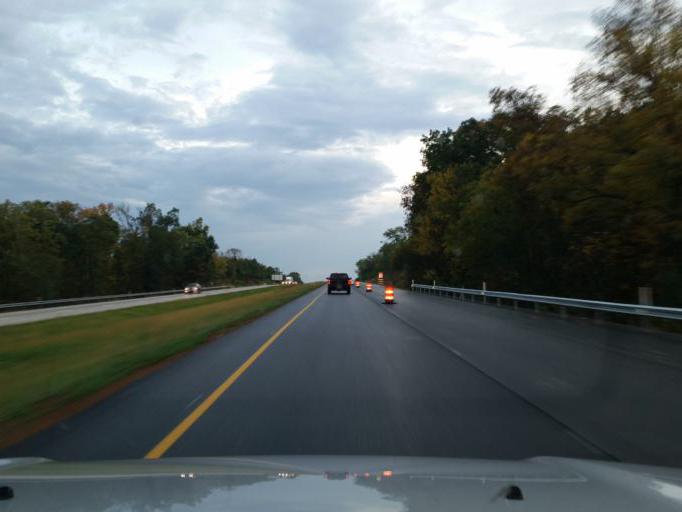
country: US
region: Maryland
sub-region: Frederick County
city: Emmitsburg
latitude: 39.7307
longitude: -77.3010
